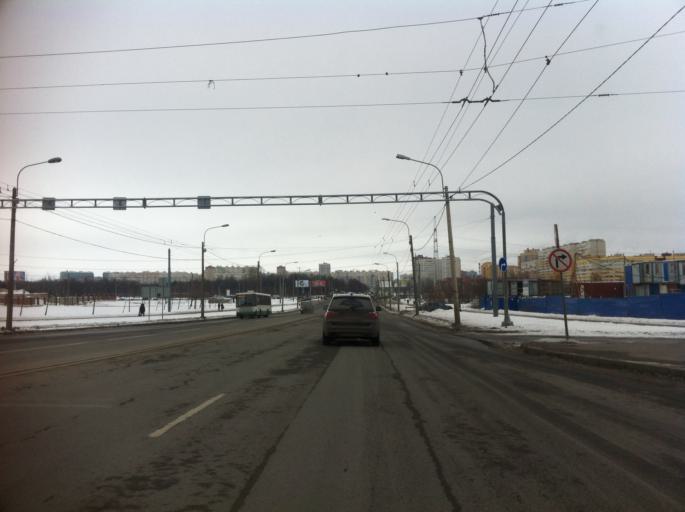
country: RU
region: St.-Petersburg
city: Uritsk
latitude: 59.8430
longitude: 30.1756
